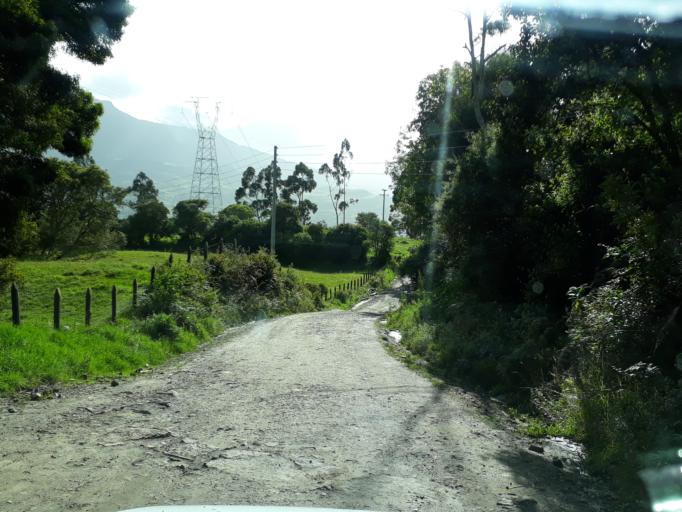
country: CO
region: Cundinamarca
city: Junin
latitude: 4.7836
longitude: -73.6804
